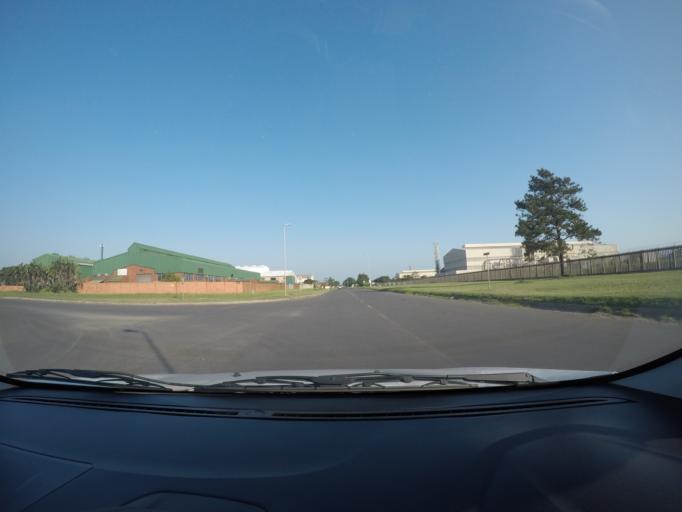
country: ZA
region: KwaZulu-Natal
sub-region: uThungulu District Municipality
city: Richards Bay
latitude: -28.7521
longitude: 32.0202
